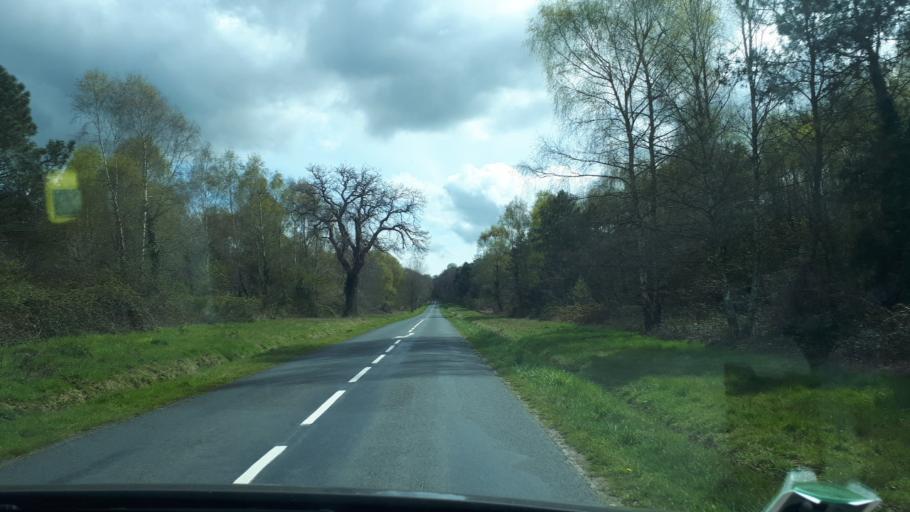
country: FR
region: Pays de la Loire
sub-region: Departement de la Sarthe
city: Challes
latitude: 47.8718
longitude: 0.3958
